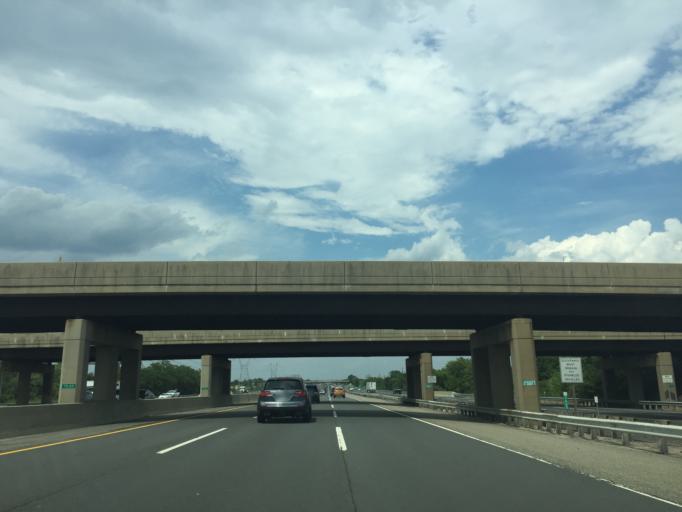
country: US
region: New Jersey
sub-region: Middlesex County
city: Jamesburg
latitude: 40.3730
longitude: -74.4638
